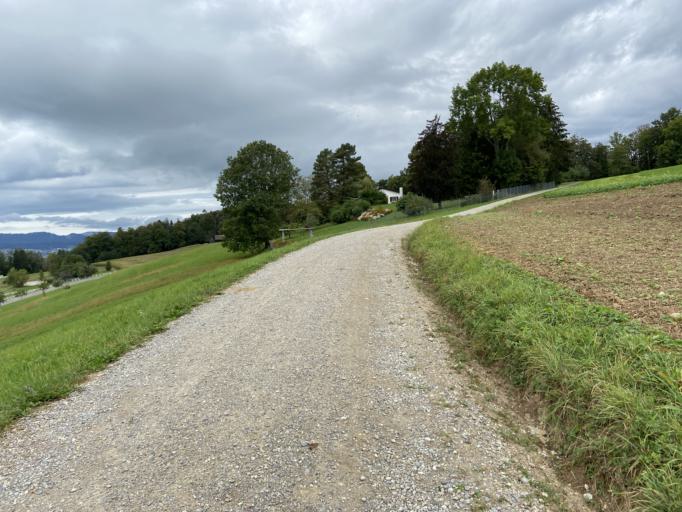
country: CH
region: Zurich
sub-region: Bezirk Meilen
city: Stafa
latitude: 47.2554
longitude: 8.7225
